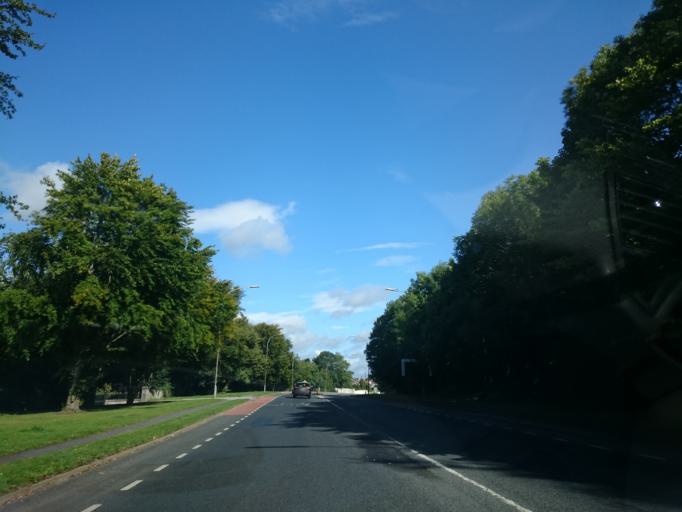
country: IE
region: Leinster
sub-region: Kilkenny
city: Kilkenny
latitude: 52.6709
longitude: -7.2531
